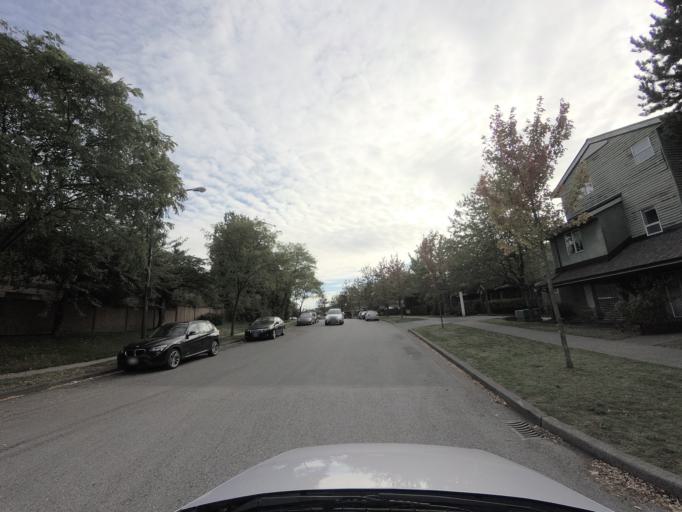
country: CA
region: British Columbia
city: Vancouver
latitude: 49.2355
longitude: -123.0398
